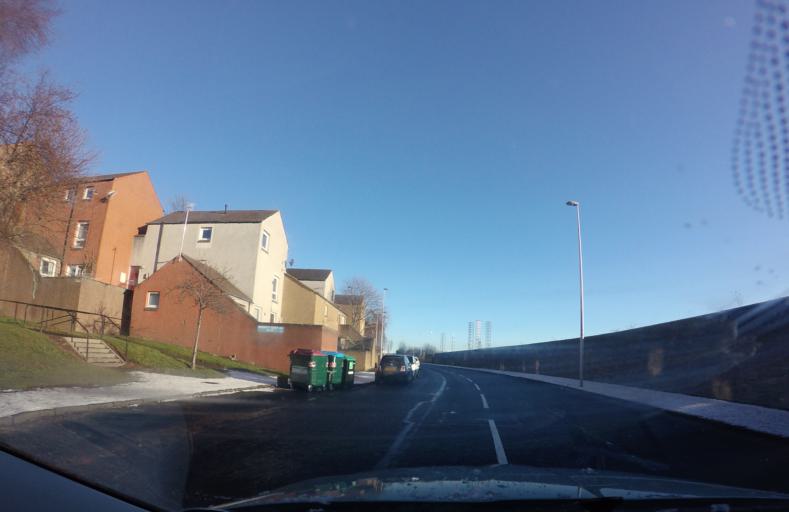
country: GB
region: Scotland
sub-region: Dundee City
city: Dundee
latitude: 56.4664
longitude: -2.9550
